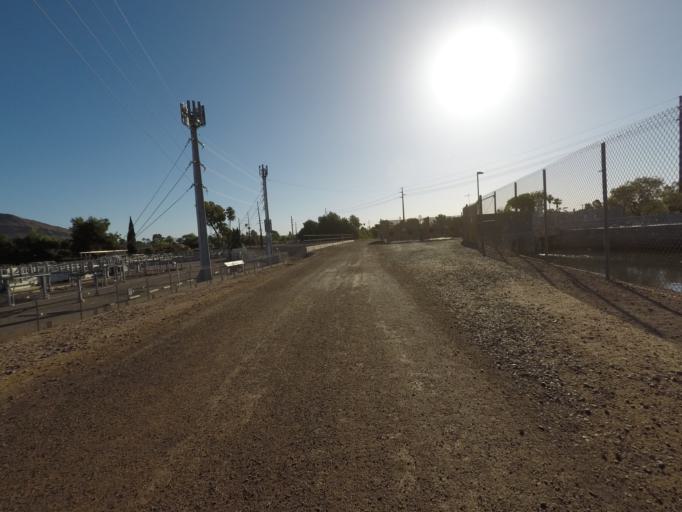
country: US
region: Arizona
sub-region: Maricopa County
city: Paradise Valley
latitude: 33.4901
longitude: -111.9591
